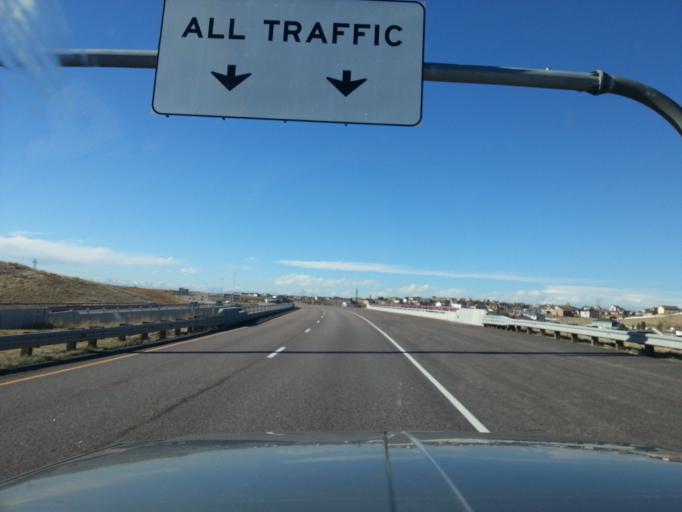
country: US
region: Colorado
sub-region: Adams County
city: Todd Creek
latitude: 39.9513
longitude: -104.8654
